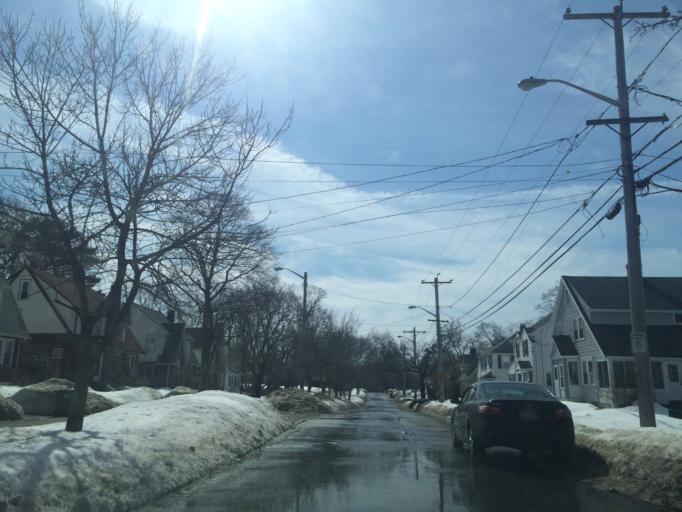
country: US
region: Massachusetts
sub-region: Middlesex County
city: Medford
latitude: 42.4295
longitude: -71.1102
